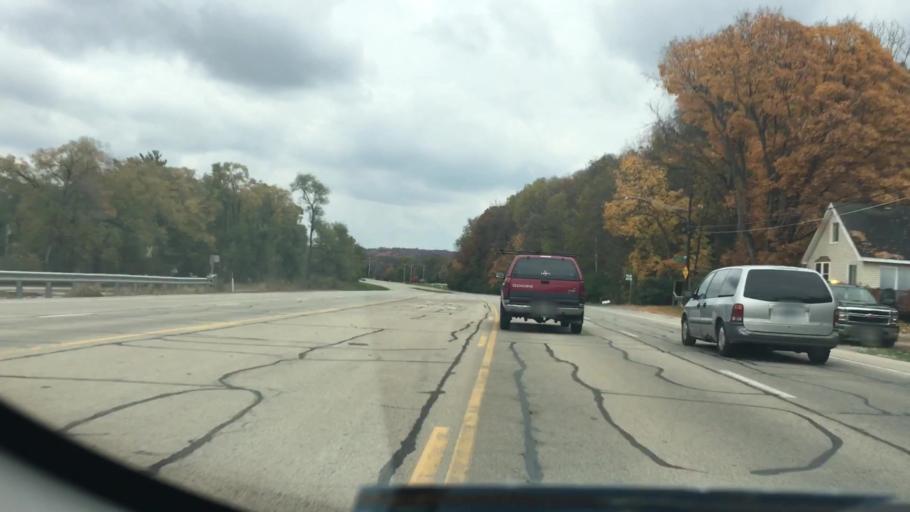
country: US
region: Illinois
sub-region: Peoria County
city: Peoria Heights
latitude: 40.7804
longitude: -89.5772
